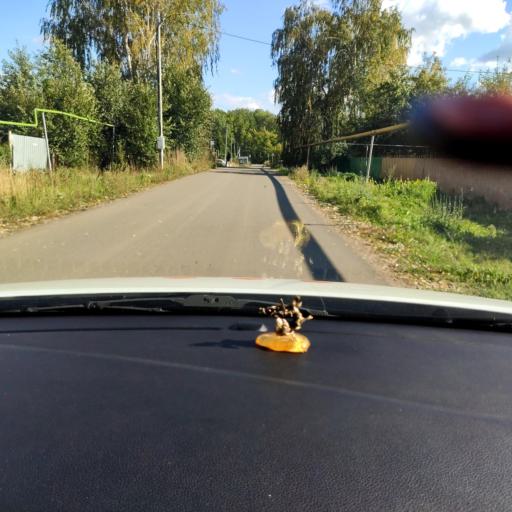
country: RU
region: Tatarstan
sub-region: Gorod Kazan'
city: Kazan
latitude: 55.7002
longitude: 49.0889
